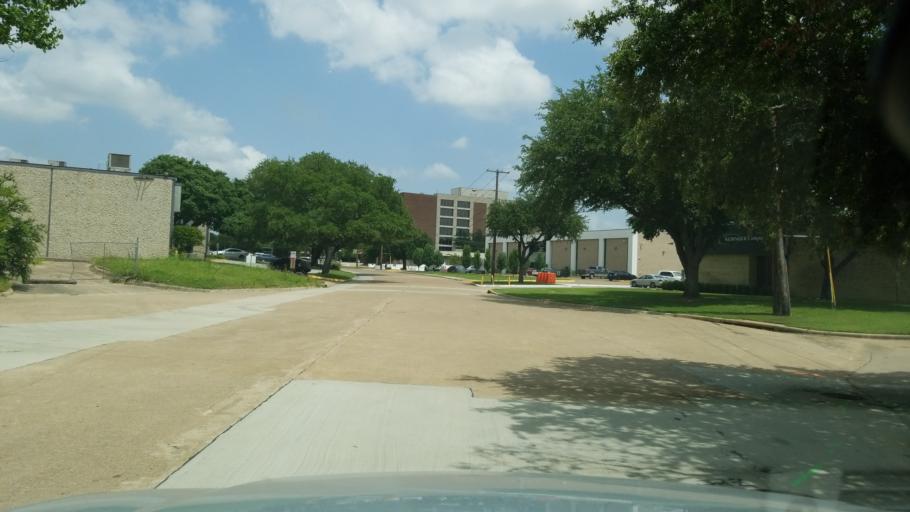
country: US
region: Texas
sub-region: Dallas County
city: University Park
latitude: 32.8245
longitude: -96.8627
